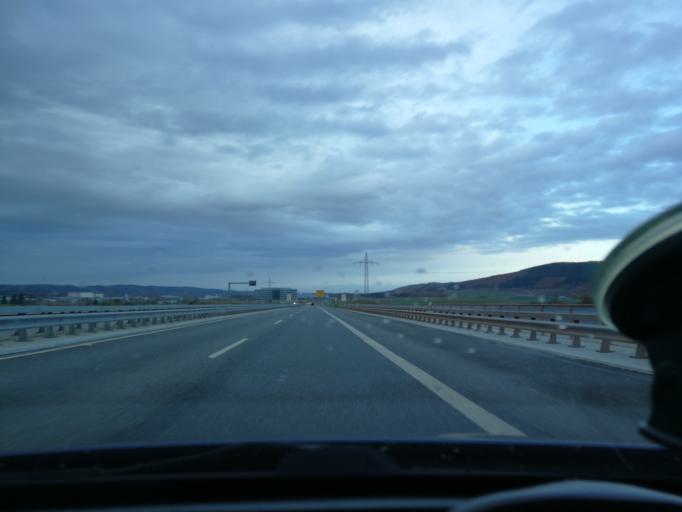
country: DE
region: Rheinland-Pfalz
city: Altrich
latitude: 49.9563
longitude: 6.9338
